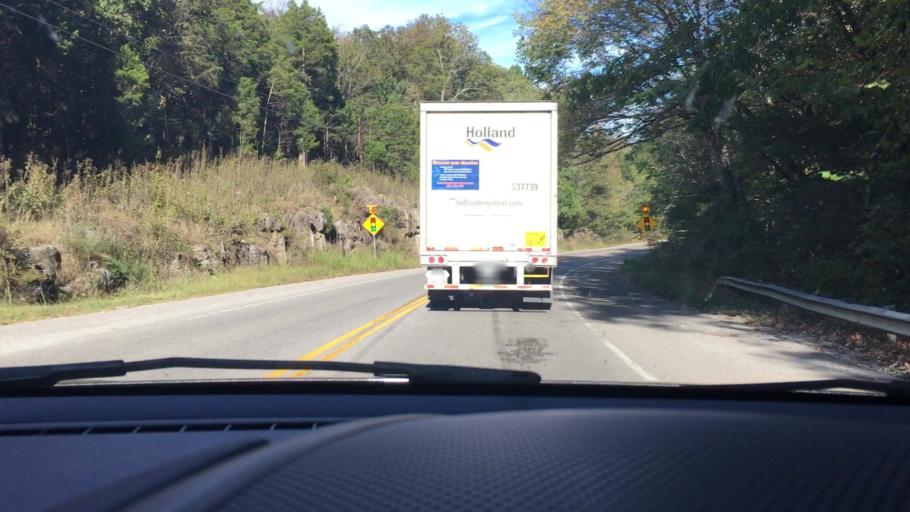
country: US
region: Tennessee
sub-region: Montgomery County
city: Clarksville
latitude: 36.4727
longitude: -87.3799
